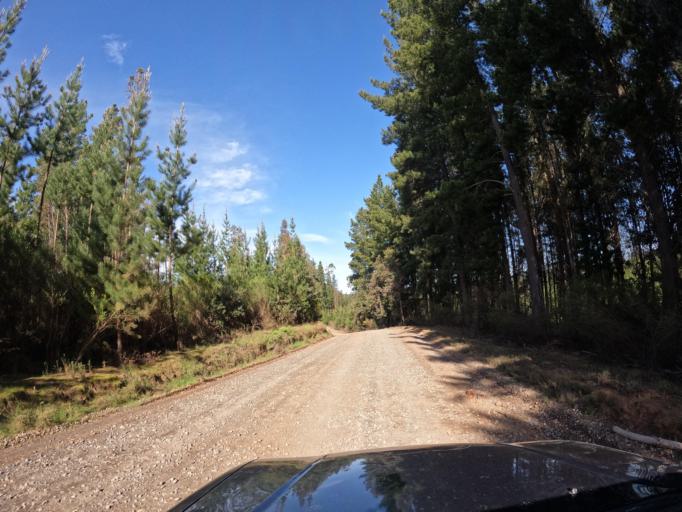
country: CL
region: Biobio
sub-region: Provincia de Biobio
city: La Laja
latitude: -37.0835
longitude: -72.7826
